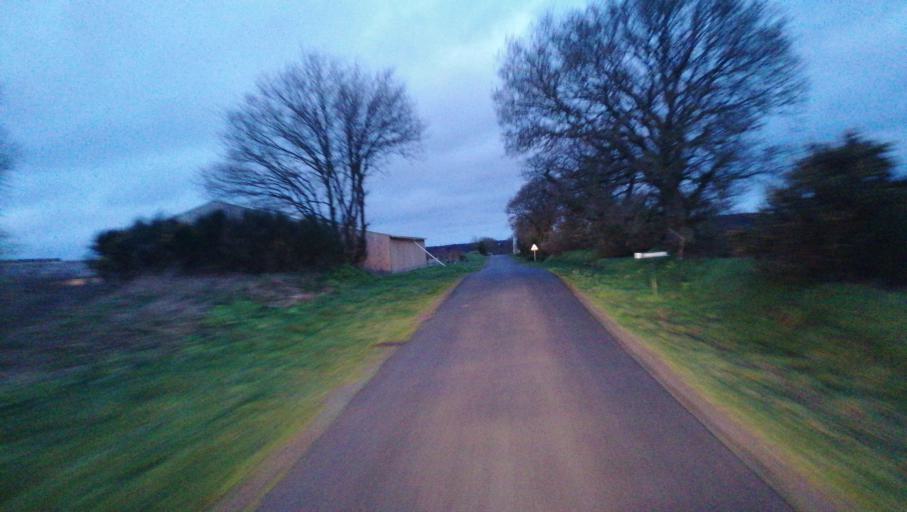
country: FR
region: Brittany
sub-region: Departement des Cotes-d'Armor
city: Plehedel
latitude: 48.6721
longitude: -3.0384
